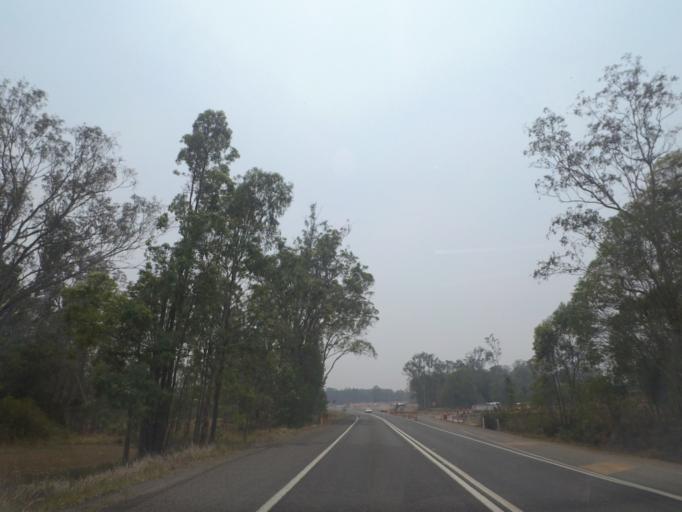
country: AU
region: New South Wales
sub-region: Clarence Valley
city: Maclean
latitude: -29.5523
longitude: 153.1540
